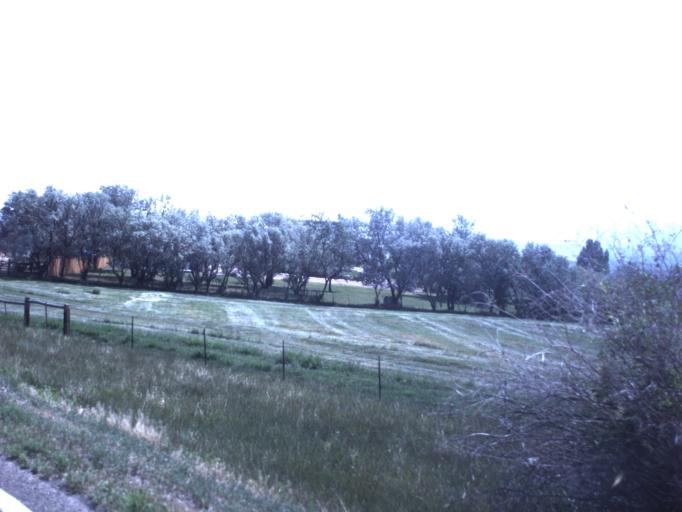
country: US
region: Utah
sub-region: Daggett County
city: Manila
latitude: 40.9777
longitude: -109.7491
